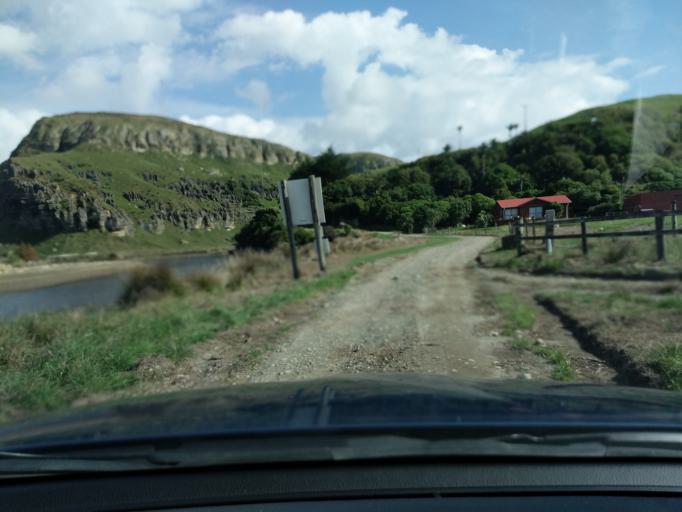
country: NZ
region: Tasman
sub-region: Tasman District
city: Takaka
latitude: -40.6431
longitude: 172.4322
